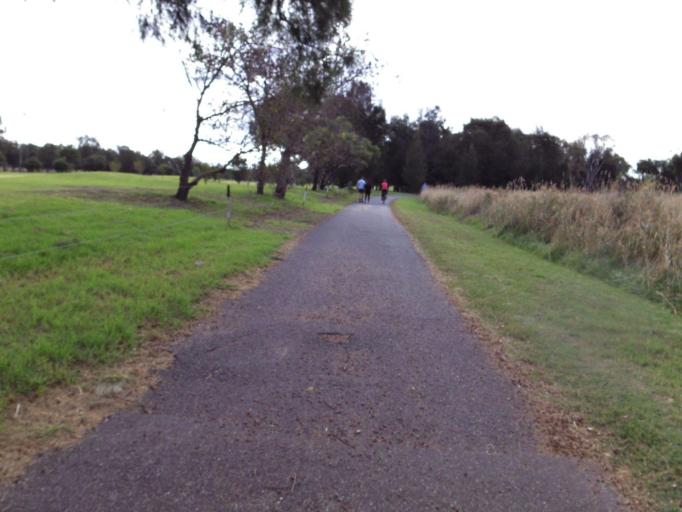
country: AU
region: Victoria
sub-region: Greater Geelong
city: Breakwater
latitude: -38.1776
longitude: 144.3609
